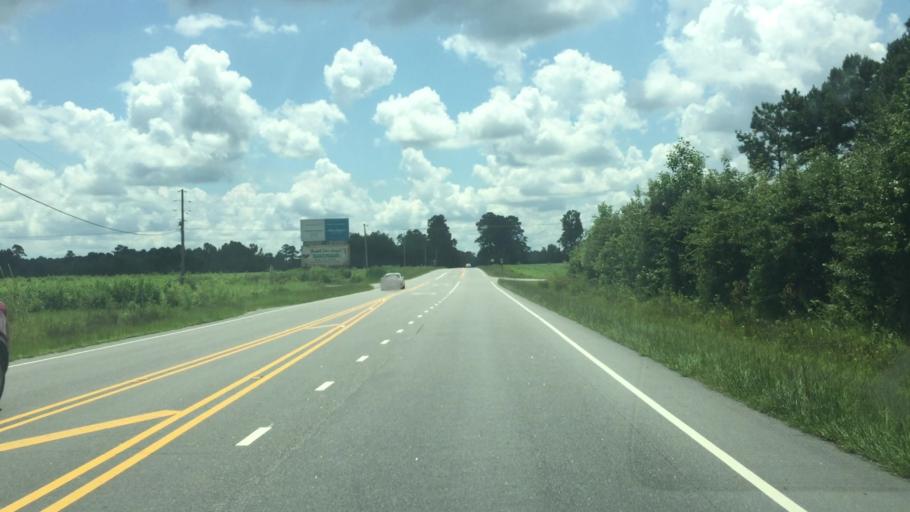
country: US
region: North Carolina
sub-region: Columbus County
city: Chadbourn
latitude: 34.2639
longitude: -78.8154
